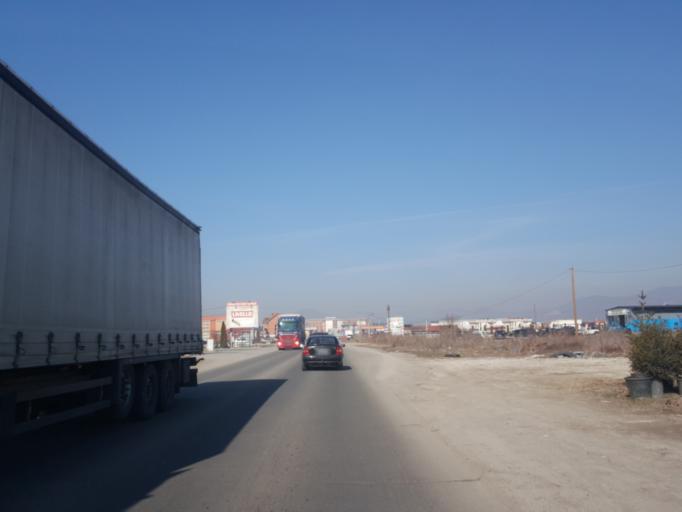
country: XK
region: Mitrovica
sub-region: Vushtrri
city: Vushtrri
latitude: 42.8109
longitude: 20.9864
